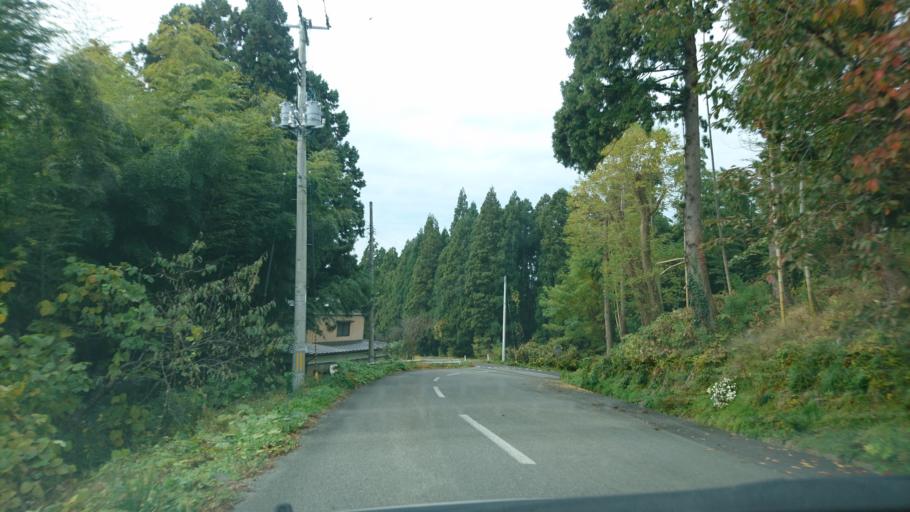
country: JP
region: Iwate
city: Ichinoseki
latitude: 38.9771
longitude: 141.1742
